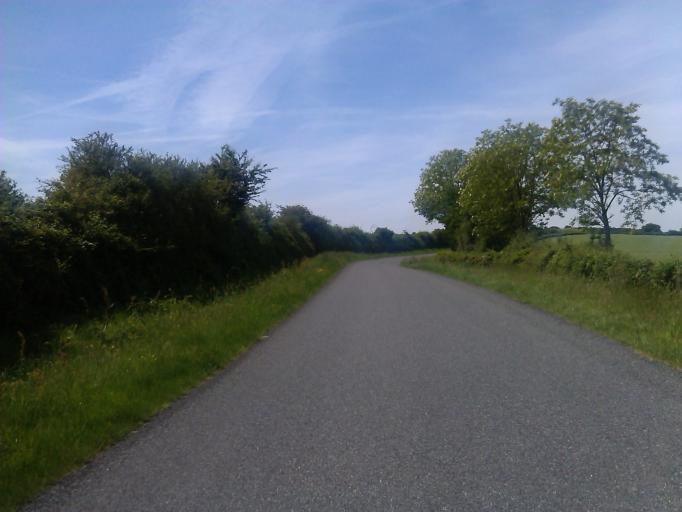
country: FR
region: Centre
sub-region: Departement du Cher
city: Orval
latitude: 46.5848
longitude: 2.4209
